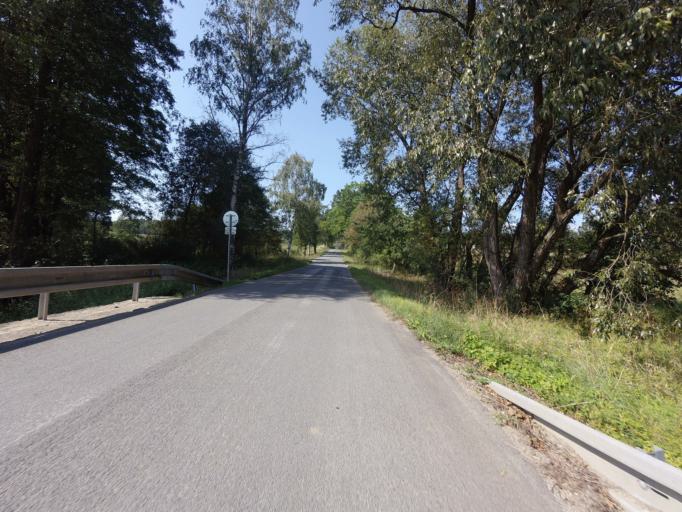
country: CZ
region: Jihocesky
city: Tyn nad Vltavou
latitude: 49.1523
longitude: 14.4424
